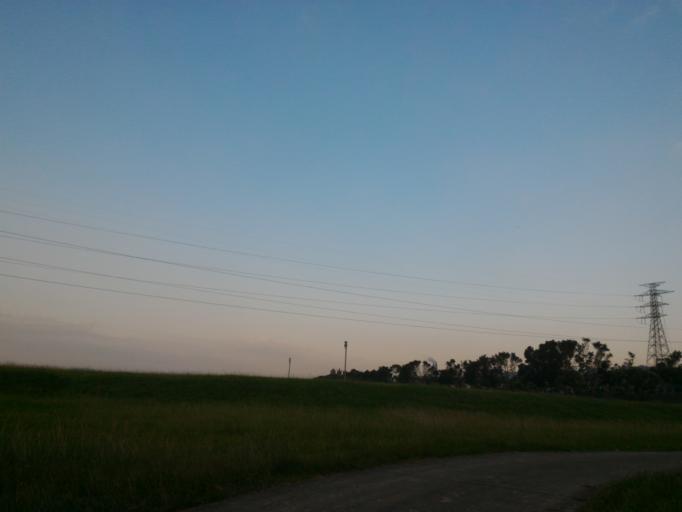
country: TW
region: Taipei
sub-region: Taipei
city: Banqiao
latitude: 24.9721
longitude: 121.4199
